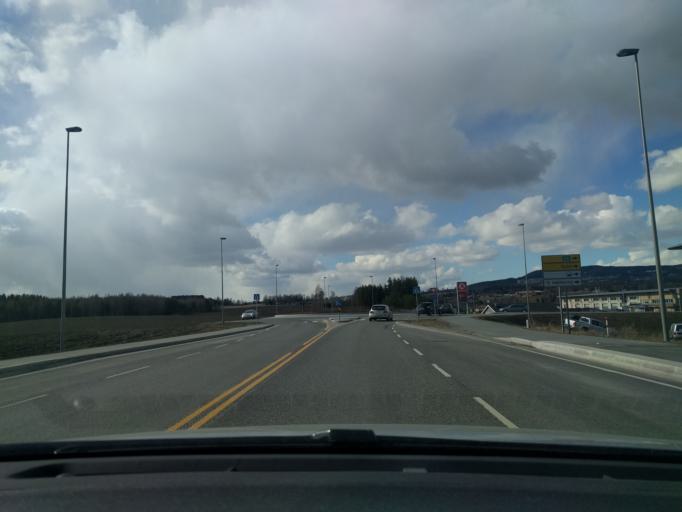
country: NO
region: Hedmark
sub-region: Hamar
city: Hamar
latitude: 60.8391
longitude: 11.0489
